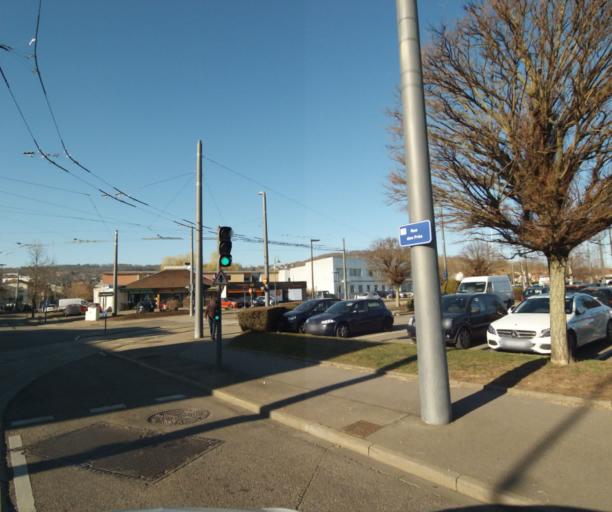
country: FR
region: Lorraine
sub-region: Departement de Meurthe-et-Moselle
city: Essey-les-Nancy
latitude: 48.7013
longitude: 6.2238
